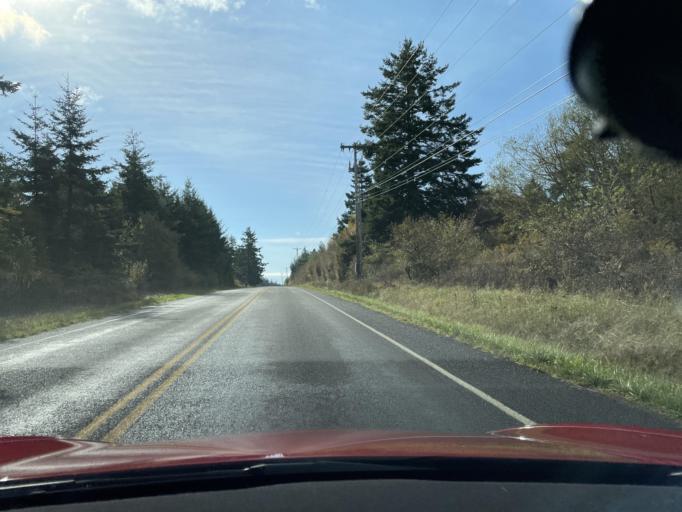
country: US
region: Washington
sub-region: San Juan County
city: Friday Harbor
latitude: 48.4807
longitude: -123.0321
